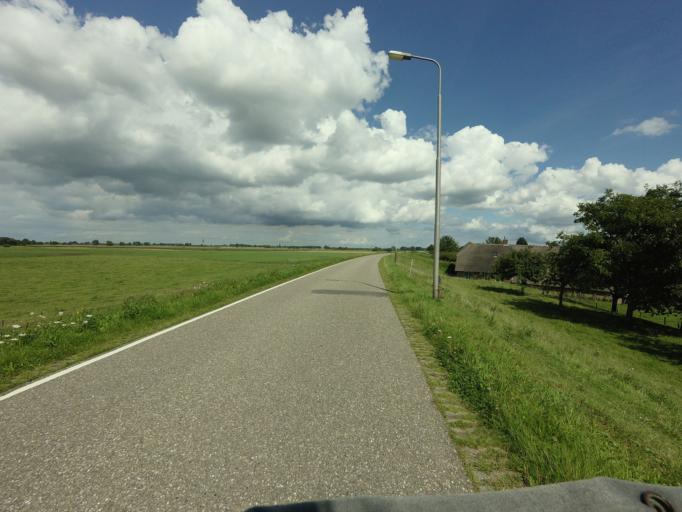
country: NL
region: Utrecht
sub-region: Gemeente IJsselstein
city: IJsselstein
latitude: 51.9732
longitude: 5.0481
